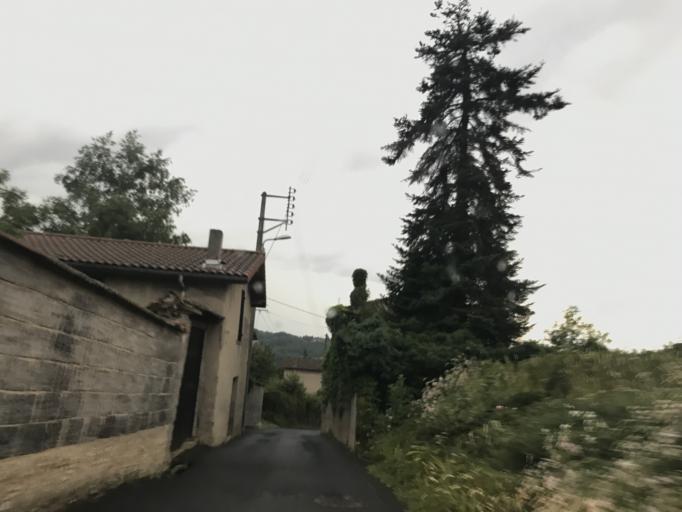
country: FR
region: Auvergne
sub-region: Departement du Puy-de-Dome
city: Thiers
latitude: 45.8553
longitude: 3.5409
